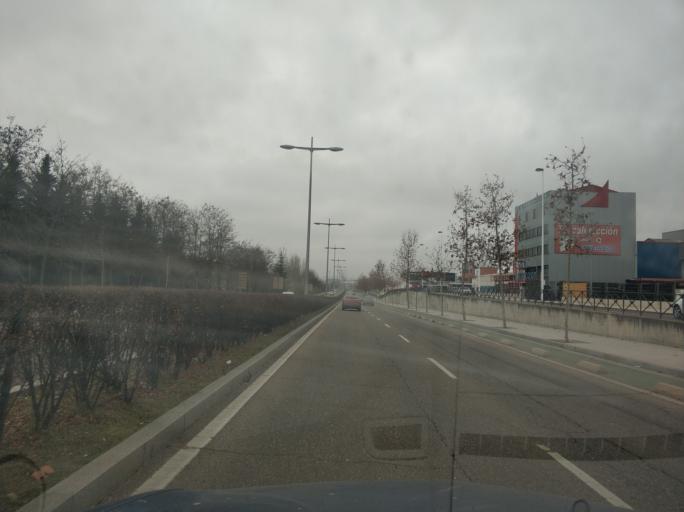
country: ES
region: Castille and Leon
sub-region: Provincia de Valladolid
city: Arroyo
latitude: 41.6270
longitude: -4.7608
